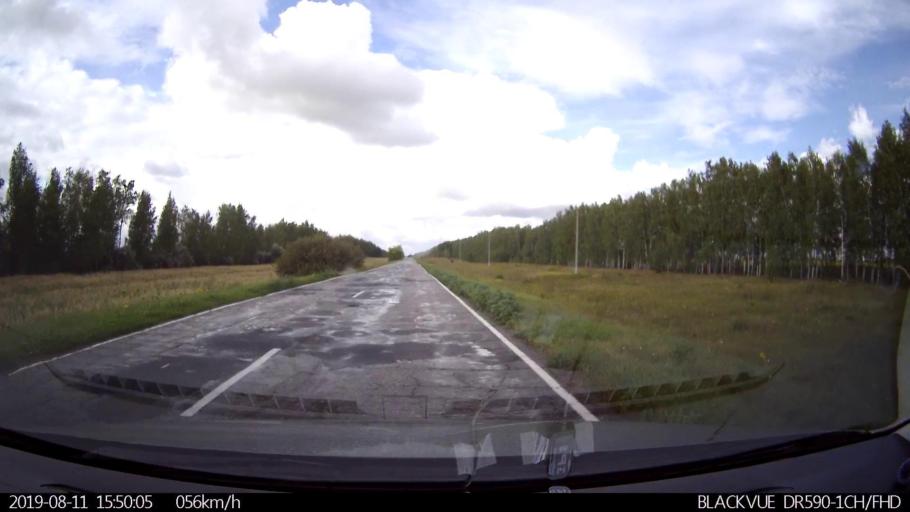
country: RU
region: Ulyanovsk
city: Ignatovka
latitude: 53.9095
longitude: 47.6557
